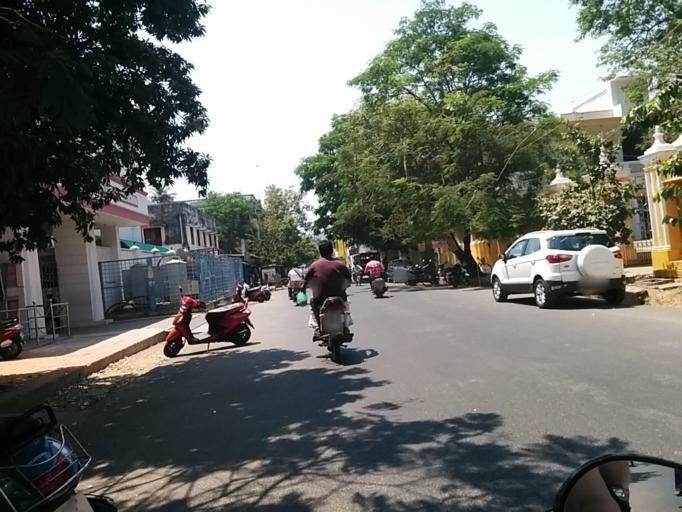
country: IN
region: Pondicherry
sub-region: Puducherry
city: Puducherry
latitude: 11.9328
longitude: 79.8307
